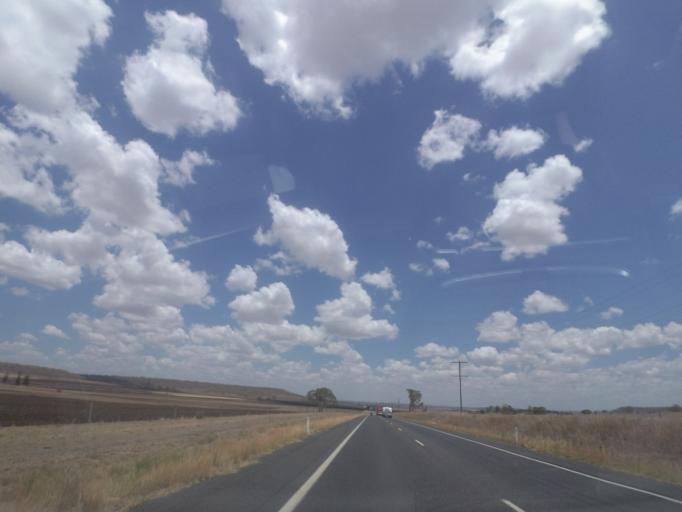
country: AU
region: Queensland
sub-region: Southern Downs
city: Warwick
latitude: -27.9972
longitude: 151.9951
